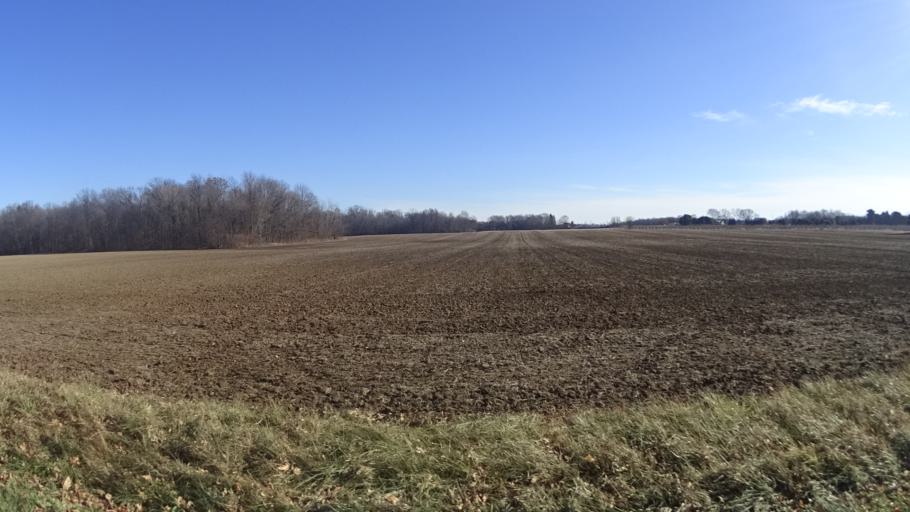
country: US
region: Ohio
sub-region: Lorain County
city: South Amherst
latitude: 41.3727
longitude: -82.3073
